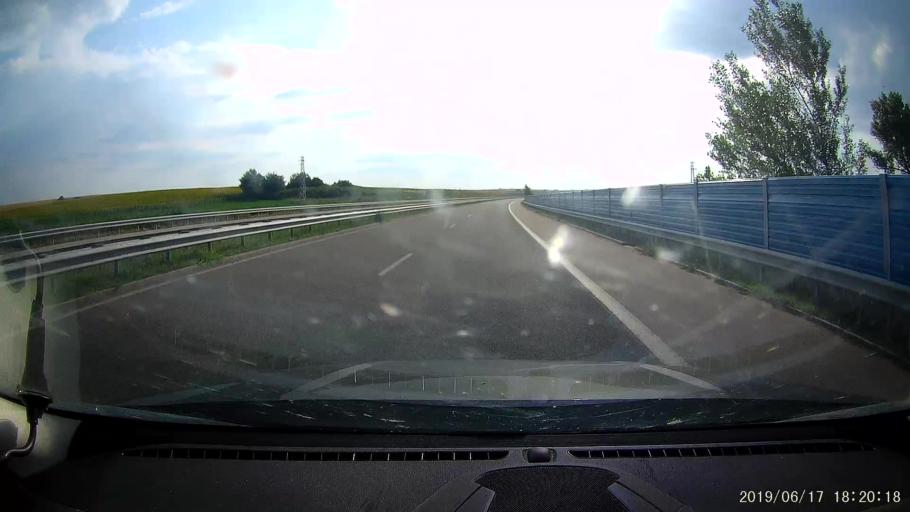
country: BG
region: Khaskovo
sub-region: Obshtina Simeonovgrad
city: Simeonovgrad
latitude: 41.9616
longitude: 25.8180
